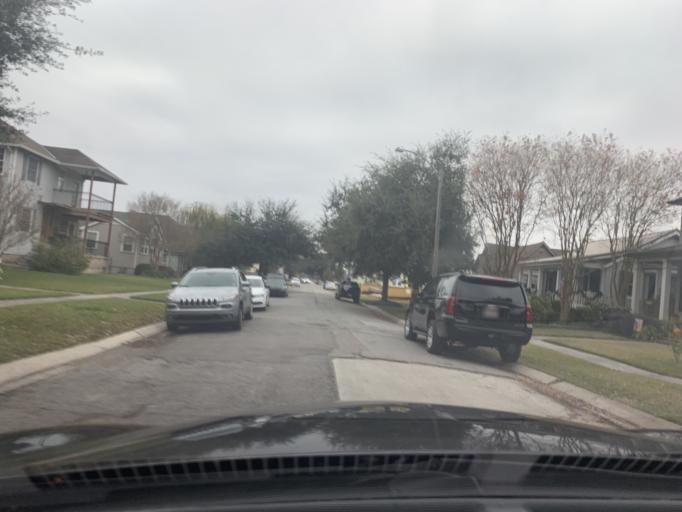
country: US
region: Louisiana
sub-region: Jefferson Parish
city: Metairie
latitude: 30.0064
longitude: -90.1112
